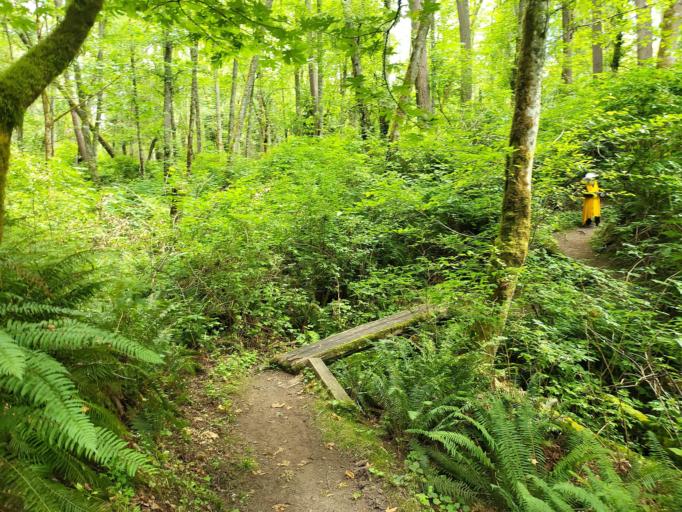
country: US
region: Washington
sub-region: King County
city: Newcastle
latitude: 47.5384
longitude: -122.1237
